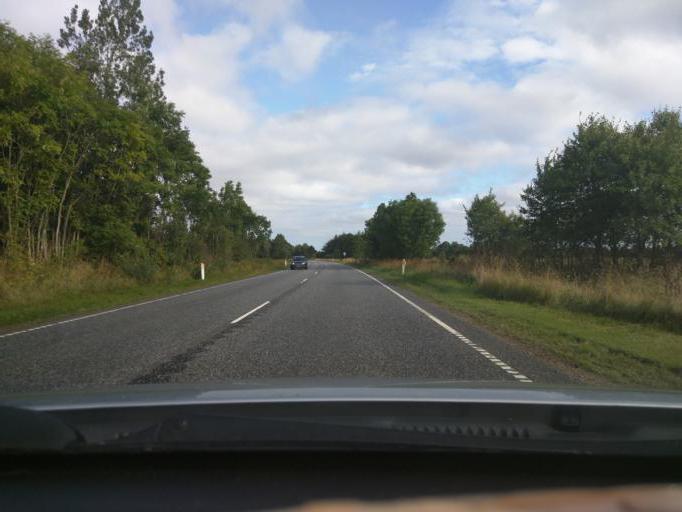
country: DK
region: Central Jutland
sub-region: Viborg Kommune
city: Viborg
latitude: 56.3794
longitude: 9.3801
